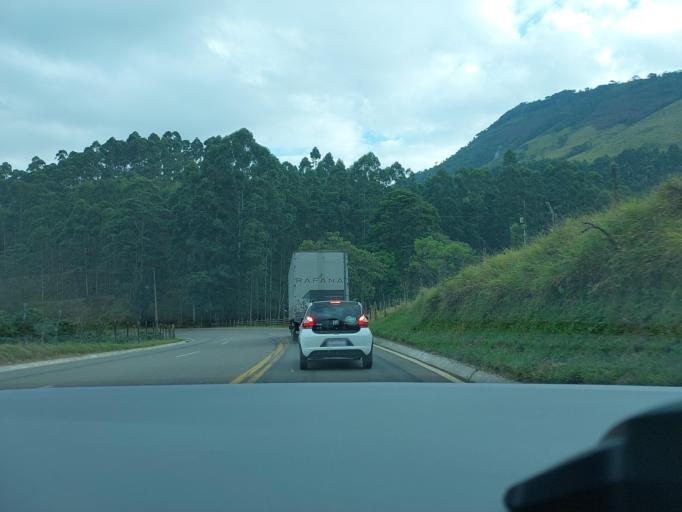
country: BR
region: Minas Gerais
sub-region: Mirai
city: Mirai
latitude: -20.9667
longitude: -42.5920
